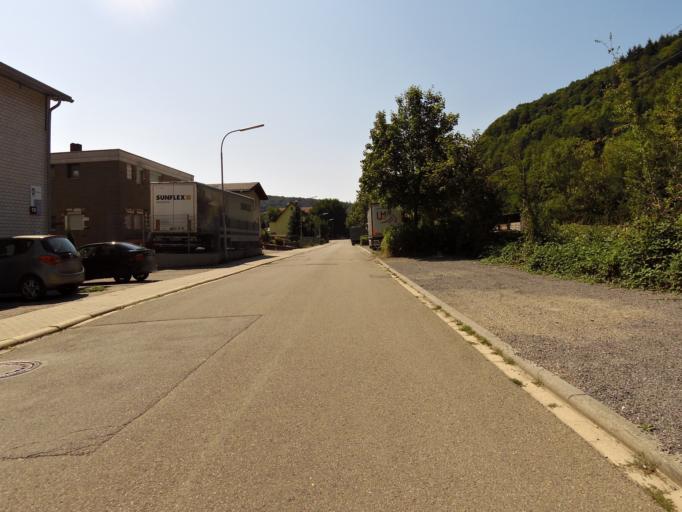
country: DE
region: Baden-Wuerttemberg
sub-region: Karlsruhe Region
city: Mosbach
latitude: 49.3620
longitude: 9.1472
